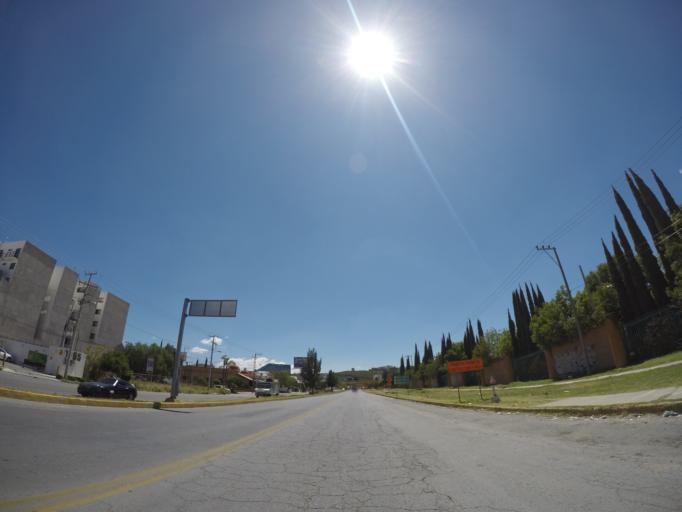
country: MX
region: San Luis Potosi
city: Escalerillas
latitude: 22.1313
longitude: -101.0350
